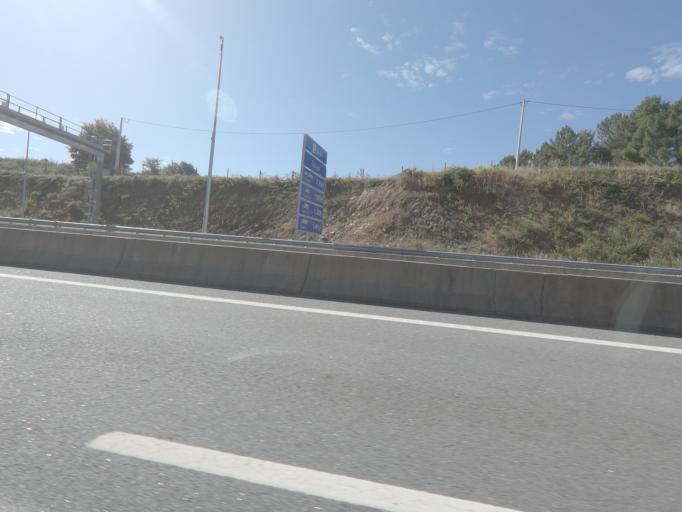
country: PT
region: Vila Real
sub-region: Vila Real
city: Vila Real
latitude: 41.2774
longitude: -7.7265
